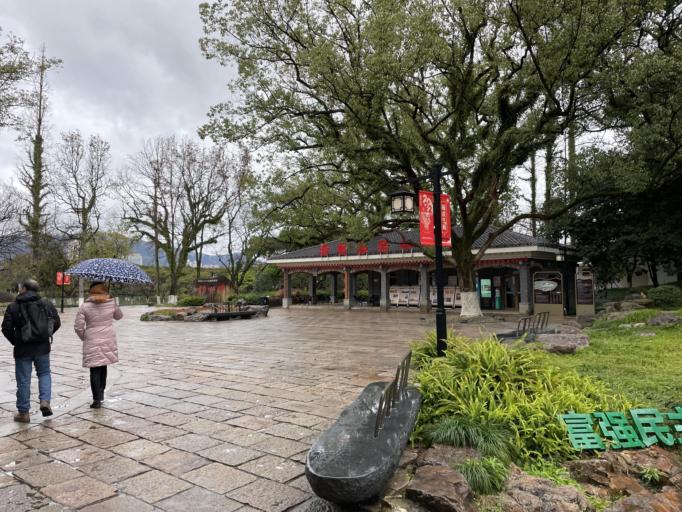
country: CN
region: Zhejiang Sheng
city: Oubei
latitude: 28.0303
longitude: 120.6436
